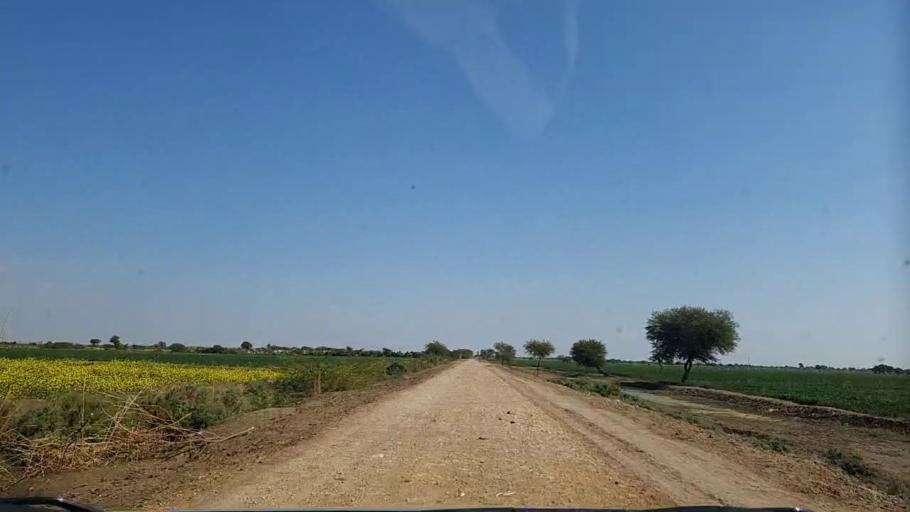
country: PK
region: Sindh
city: Pithoro
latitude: 25.6863
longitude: 69.4631
